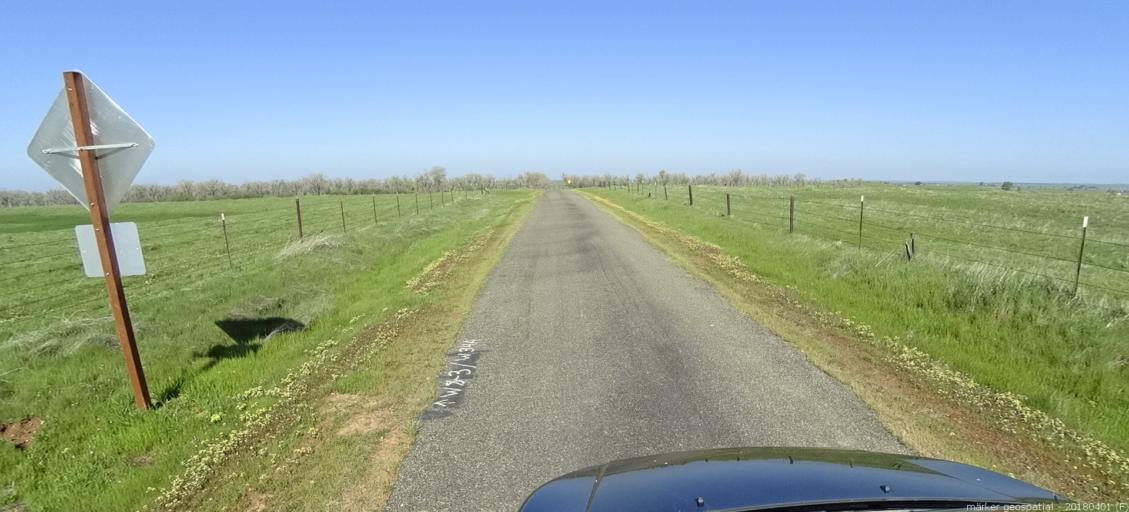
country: US
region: California
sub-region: Sacramento County
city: Rancho Murieta
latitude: 38.4562
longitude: -121.1026
